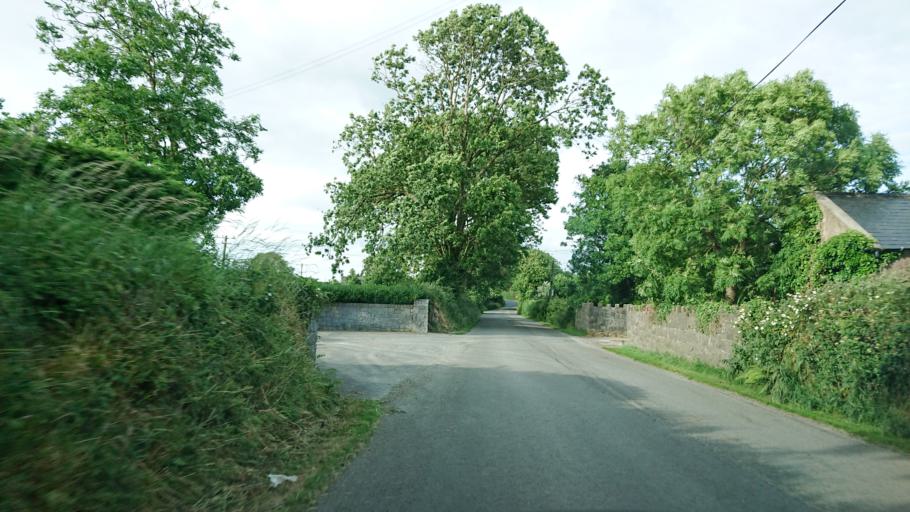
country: IE
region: Munster
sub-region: Waterford
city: Waterford
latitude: 52.2323
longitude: -7.1608
